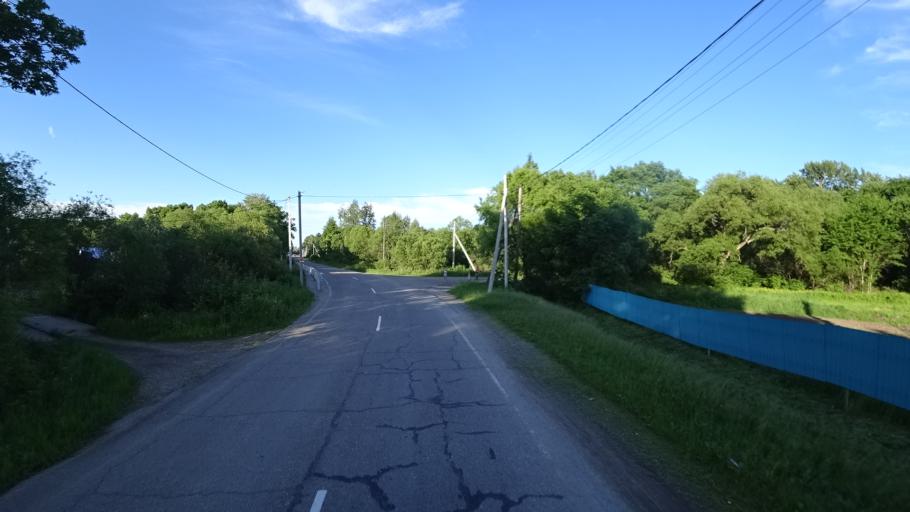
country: RU
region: Khabarovsk Krai
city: Khor
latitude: 47.8530
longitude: 134.9818
